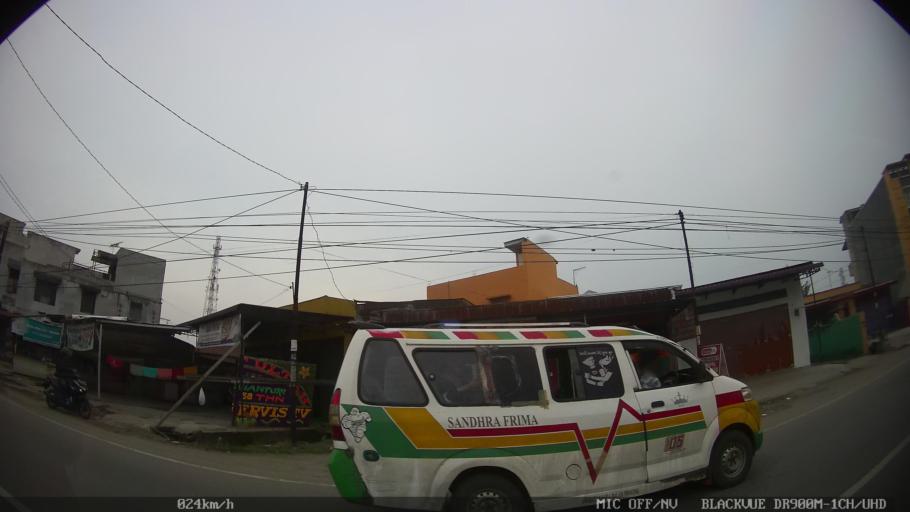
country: ID
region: North Sumatra
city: Deli Tua
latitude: 3.5458
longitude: 98.7185
